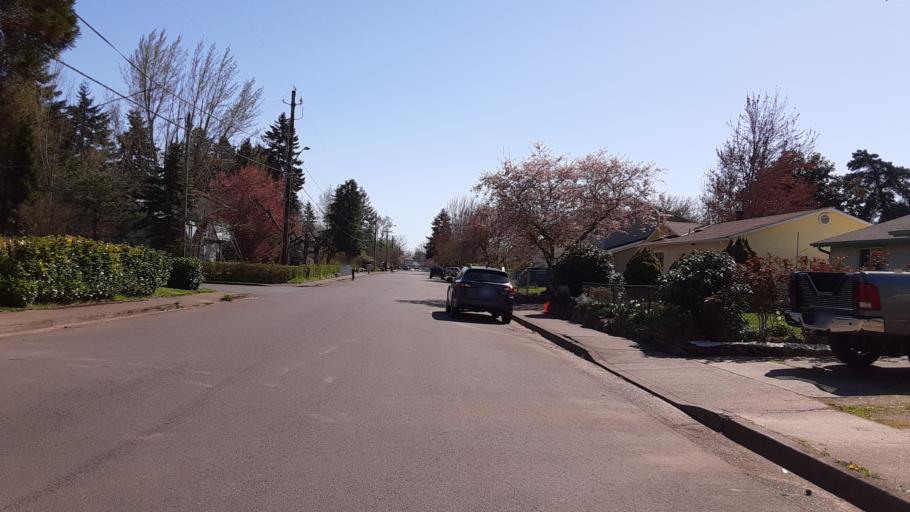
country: US
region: Oregon
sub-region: Benton County
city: Corvallis
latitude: 44.5421
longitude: -123.2605
